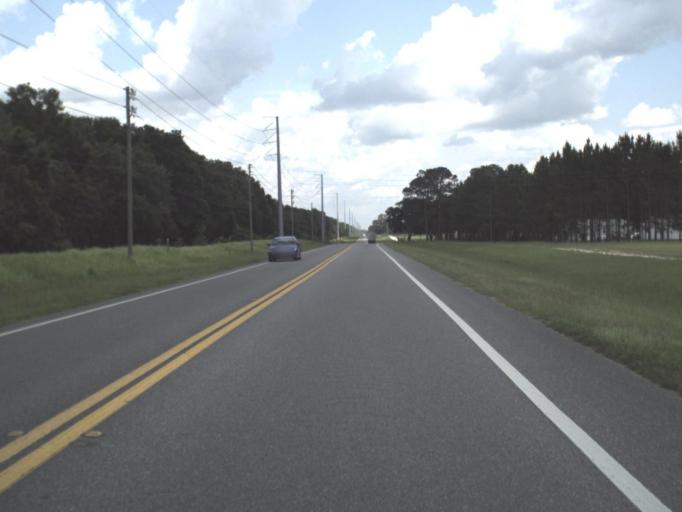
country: US
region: Florida
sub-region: Gilchrist County
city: Trenton
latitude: 29.6128
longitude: -82.8693
